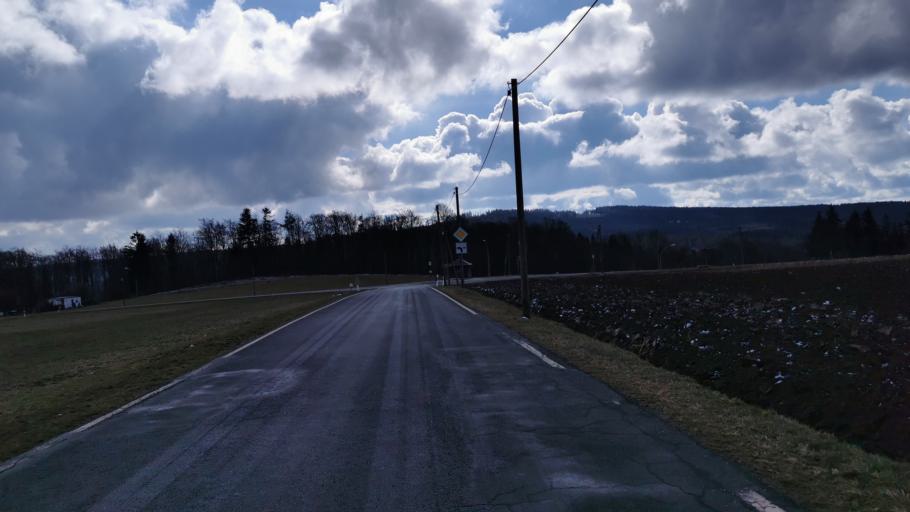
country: DE
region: Thuringia
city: Leutenberg
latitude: 50.4937
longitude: 11.4714
